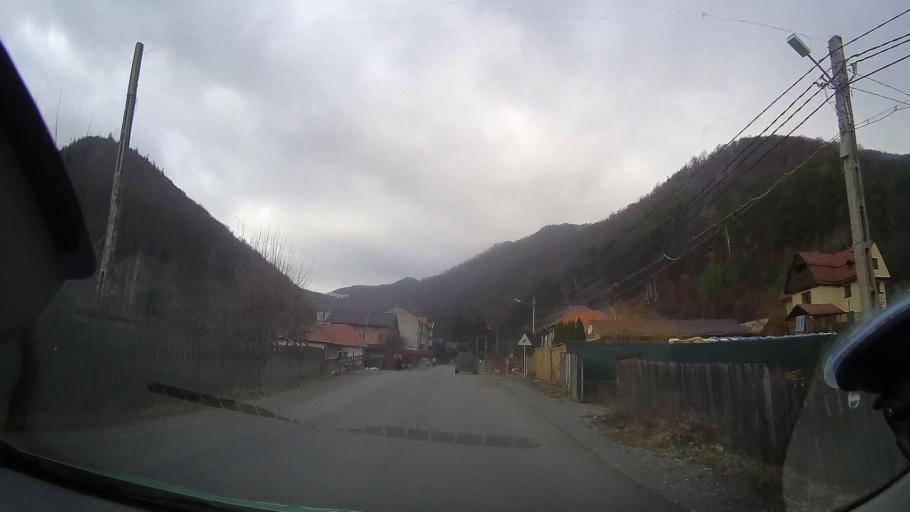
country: RO
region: Cluj
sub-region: Comuna Valea Ierii
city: Valea Ierii
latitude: 46.6475
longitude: 23.3427
